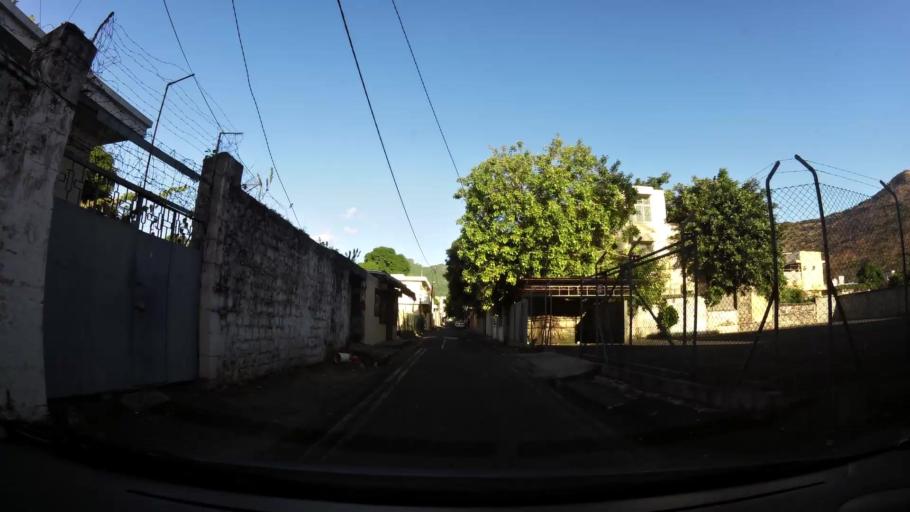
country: MU
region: Port Louis
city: Port Louis
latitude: -20.1669
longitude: 57.5008
